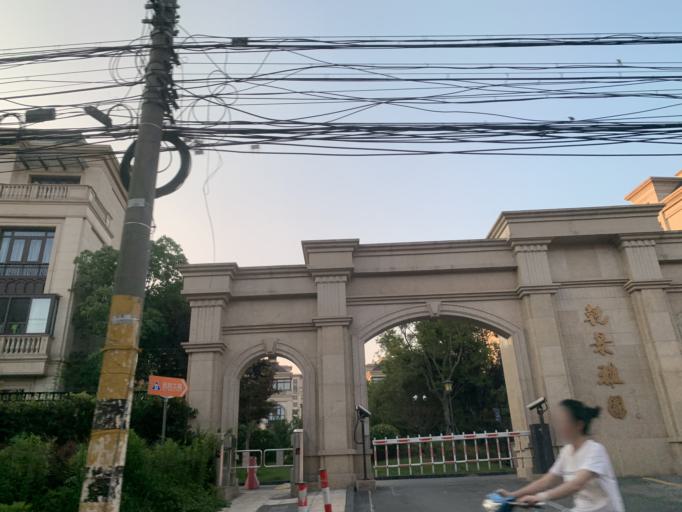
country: CN
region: Shanghai Shi
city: Huamu
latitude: 31.1870
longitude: 121.5436
